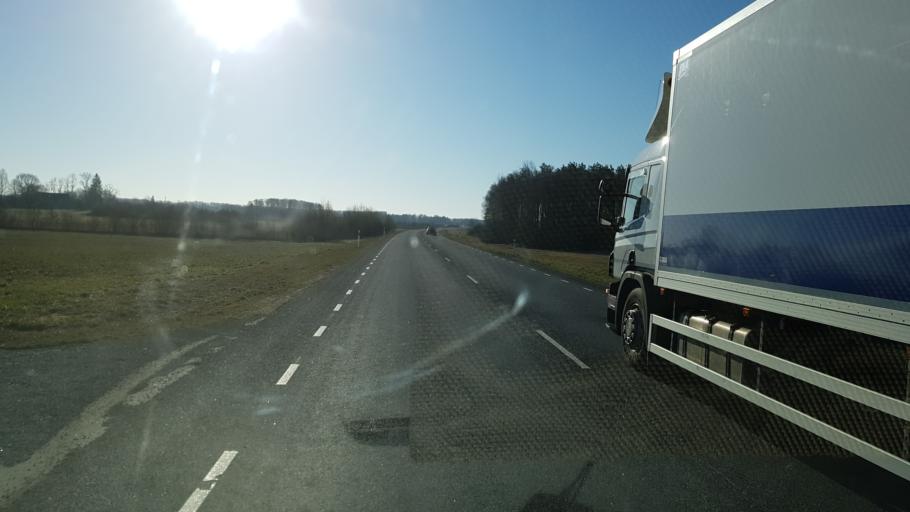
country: EE
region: Jaervamaa
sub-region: Tueri vald
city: Sarevere
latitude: 58.7774
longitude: 25.5021
